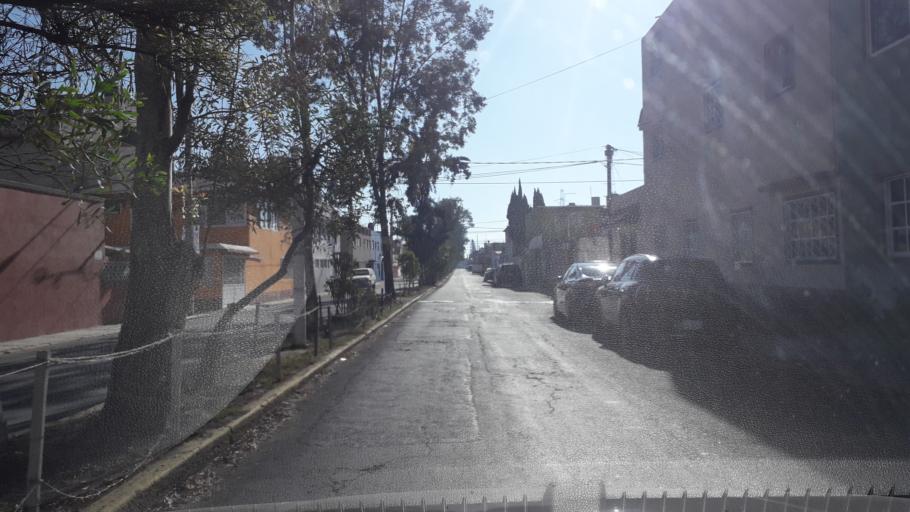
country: MX
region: Mexico City
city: Gustavo A. Madero
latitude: 19.5075
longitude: -99.0822
